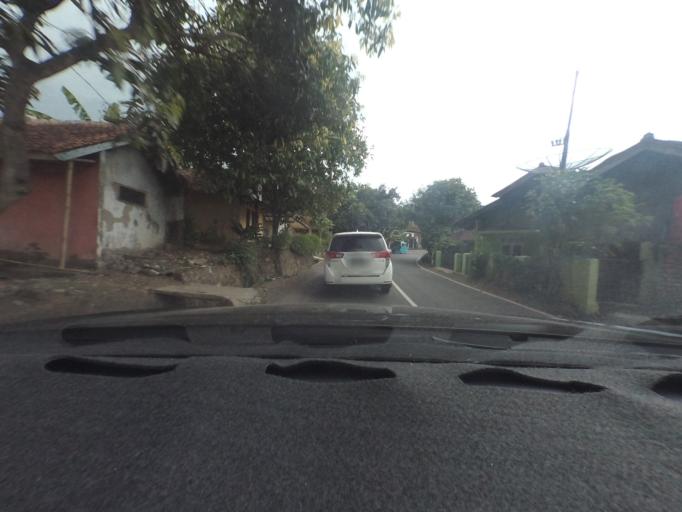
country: ID
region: West Java
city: Sindangsari
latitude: -6.9930
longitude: 106.6739
